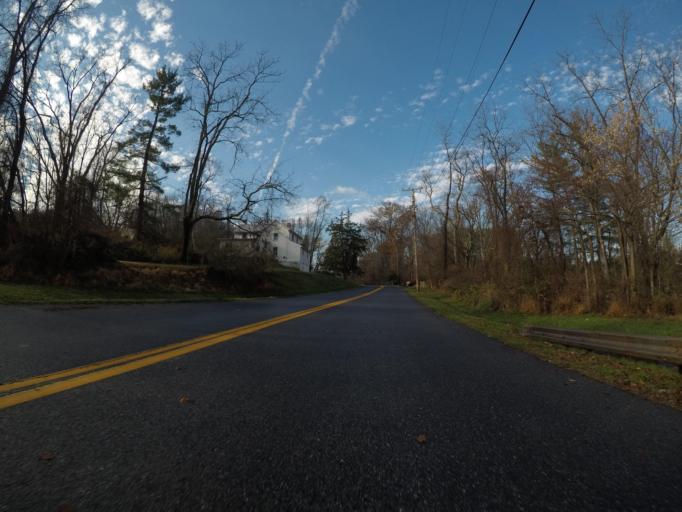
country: US
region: Maryland
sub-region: Carroll County
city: Hampstead
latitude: 39.5717
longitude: -76.8210
